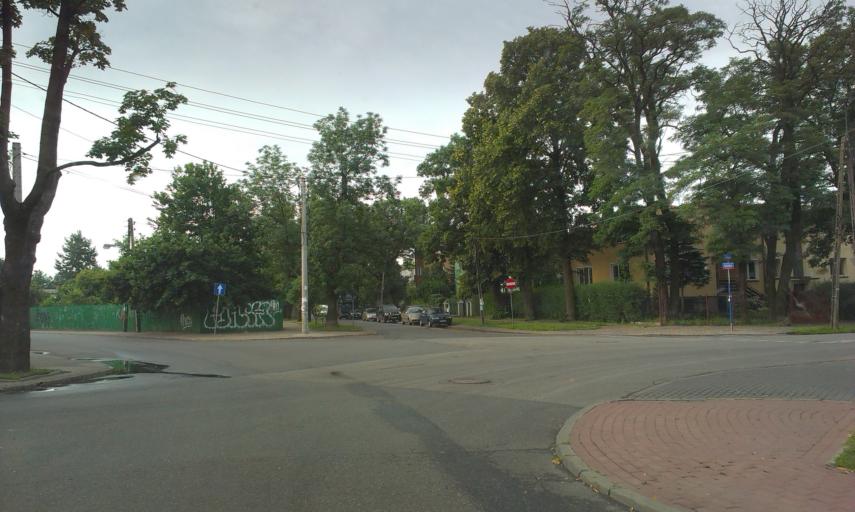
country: PL
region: Masovian Voivodeship
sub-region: Warszawa
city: Ursus
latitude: 52.1952
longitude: 20.8824
